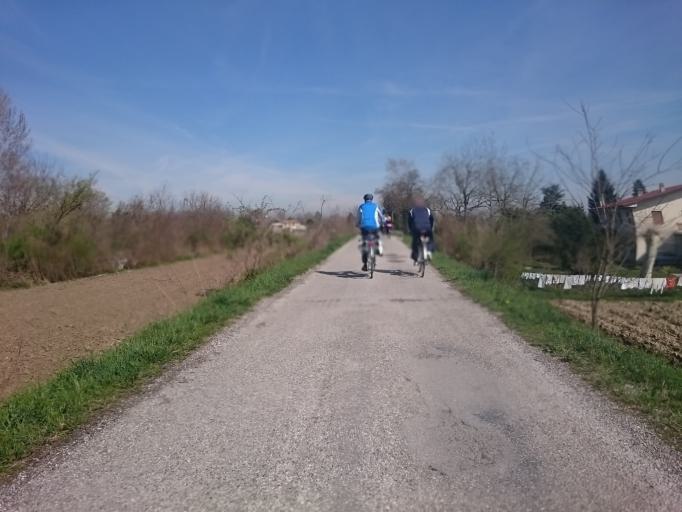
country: IT
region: Veneto
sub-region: Provincia di Padova
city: Sarmeola
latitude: 45.4267
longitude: 11.8290
